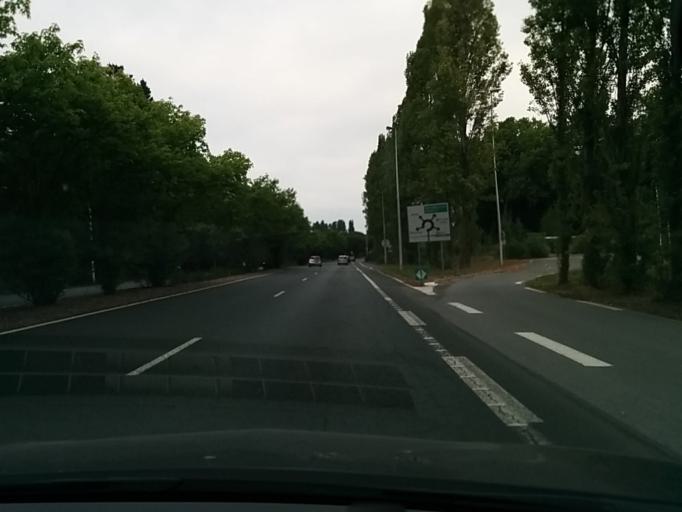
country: FR
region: Aquitaine
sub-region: Departement des Pyrenees-Atlantiques
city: Bayonne
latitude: 43.4763
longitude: -1.4908
